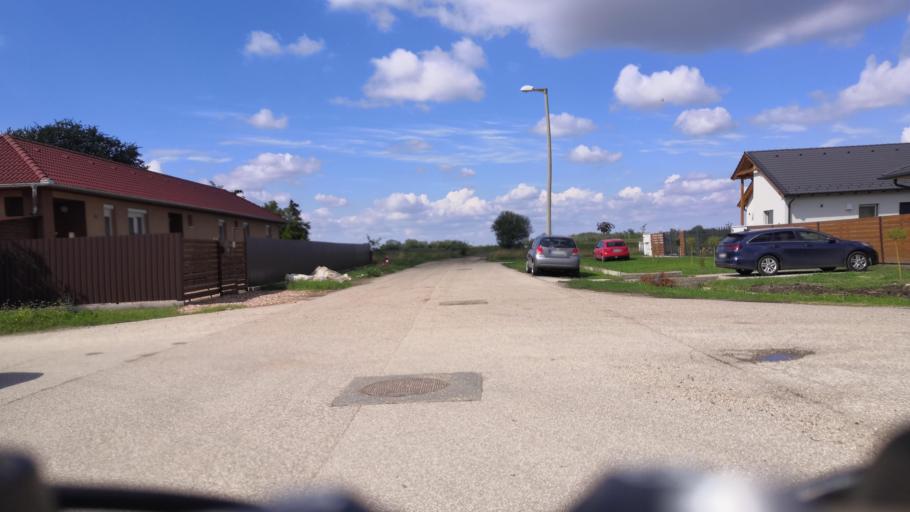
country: HU
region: Csongrad
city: Szeged
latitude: 46.2790
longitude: 20.1143
